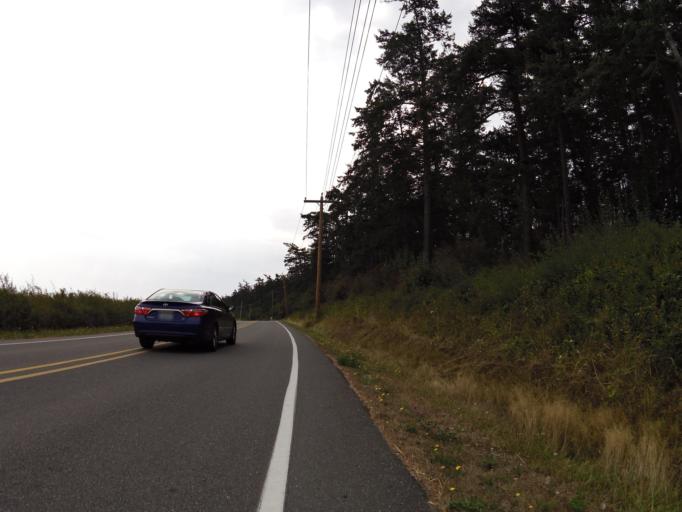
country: US
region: Washington
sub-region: Island County
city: Coupeville
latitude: 48.1862
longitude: -122.6689
